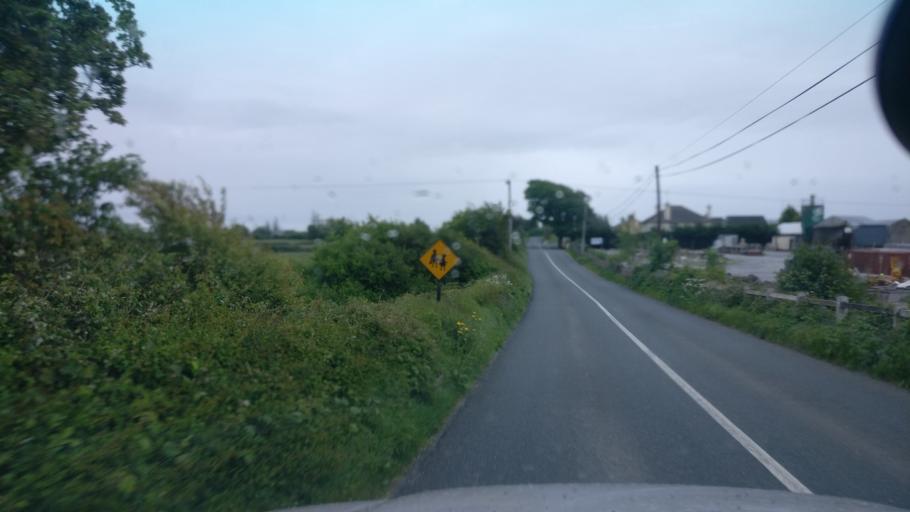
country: IE
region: Connaught
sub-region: County Galway
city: Gort
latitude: 53.0704
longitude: -8.7841
